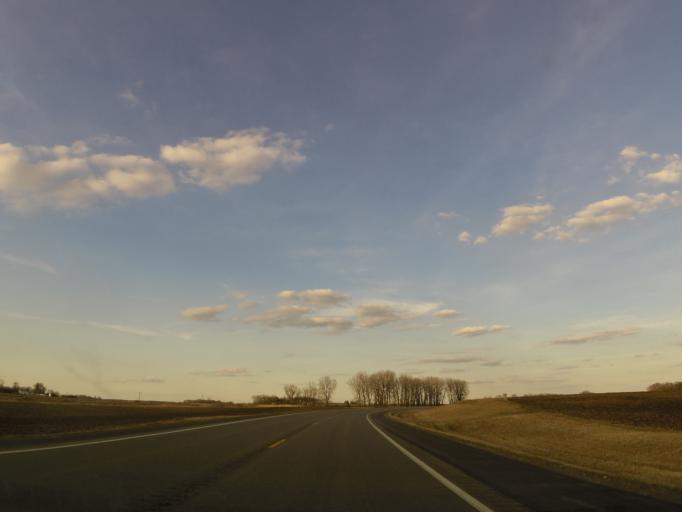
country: US
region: Minnesota
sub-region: McLeod County
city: Glencoe
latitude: 44.7369
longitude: -94.2886
